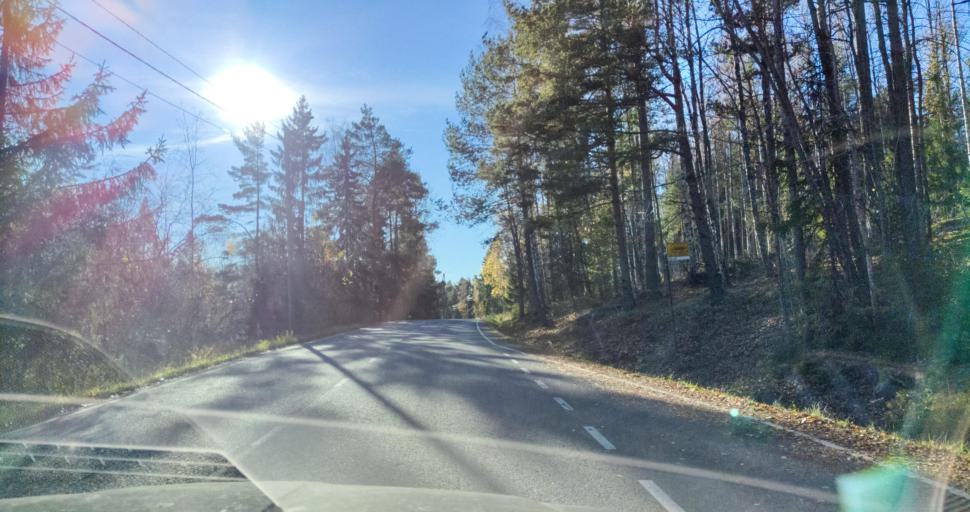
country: FI
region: Varsinais-Suomi
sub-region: Turku
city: Turku
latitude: 60.4011
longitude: 22.2070
